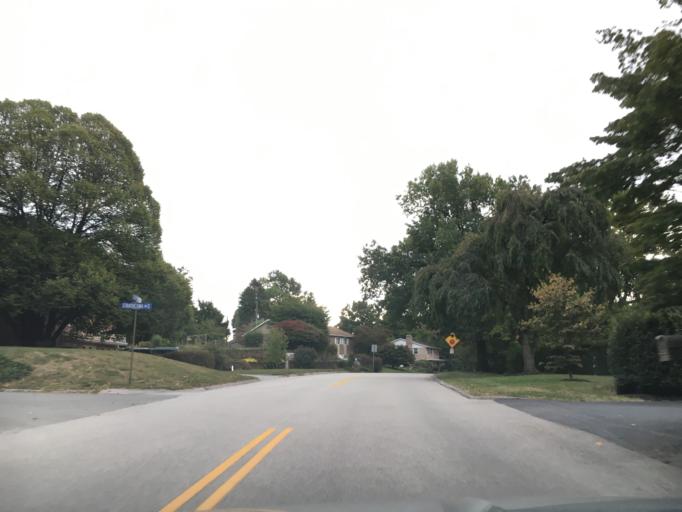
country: US
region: Pennsylvania
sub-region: York County
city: Valley View
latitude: 39.9430
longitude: -76.7114
